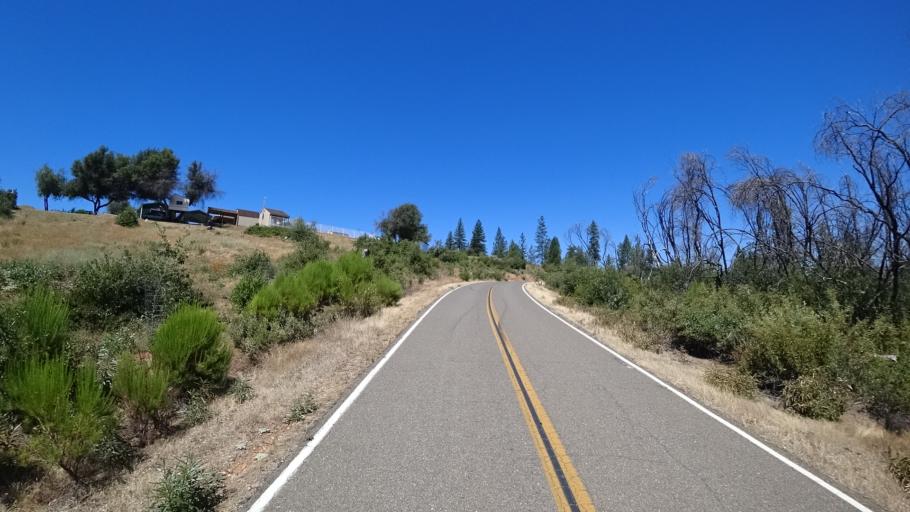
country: US
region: California
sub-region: Calaveras County
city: Mountain Ranch
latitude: 38.2072
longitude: -120.5211
